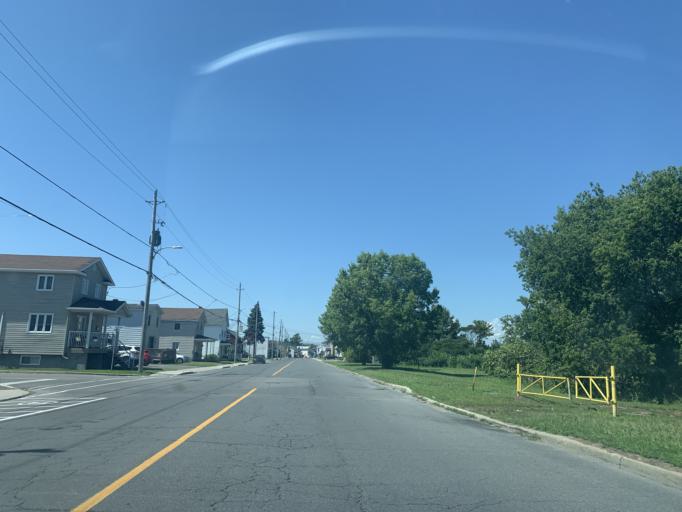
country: CA
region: Ontario
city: Hawkesbury
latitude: 45.6078
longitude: -74.5862
